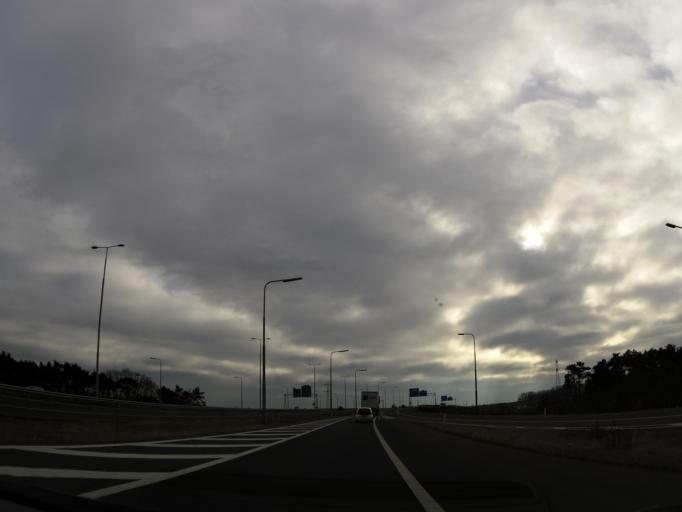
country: NL
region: Limburg
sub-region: Gemeente Venlo
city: Venlo
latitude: 51.3902
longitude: 6.1271
